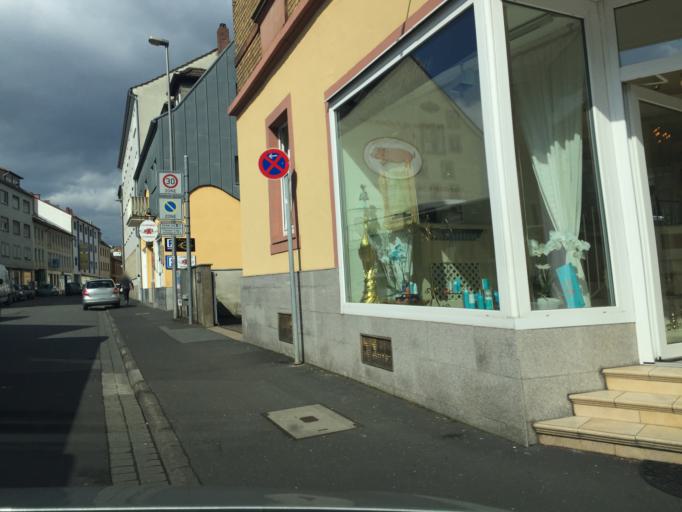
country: DE
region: Bavaria
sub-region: Regierungsbezirk Unterfranken
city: Aschaffenburg
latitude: 49.9819
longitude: 9.1479
